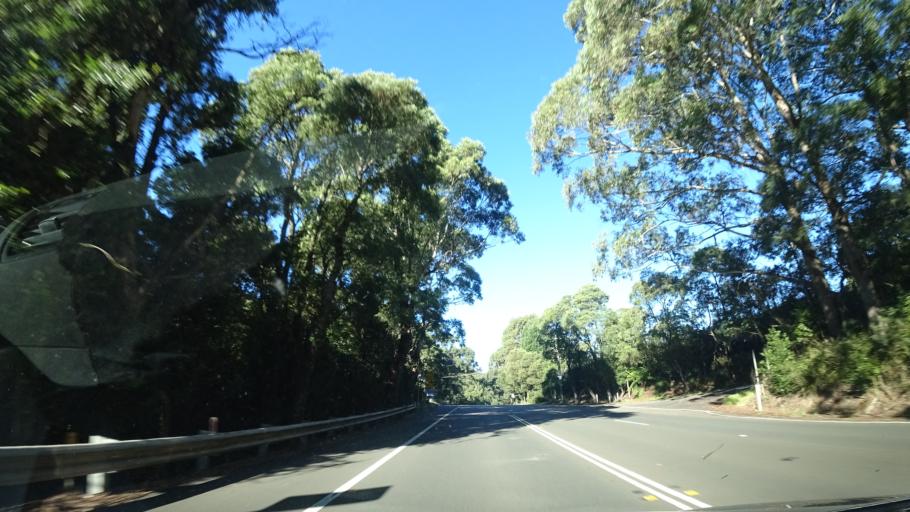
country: AU
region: New South Wales
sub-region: Blue Mountains Municipality
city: Blackheath
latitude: -33.5460
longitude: 150.4251
